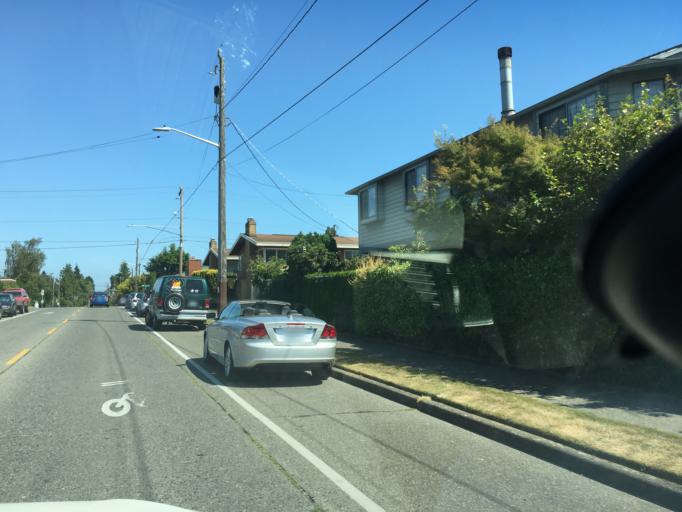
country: US
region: Washington
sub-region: King County
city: Shoreline
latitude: 47.6906
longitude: -122.3898
